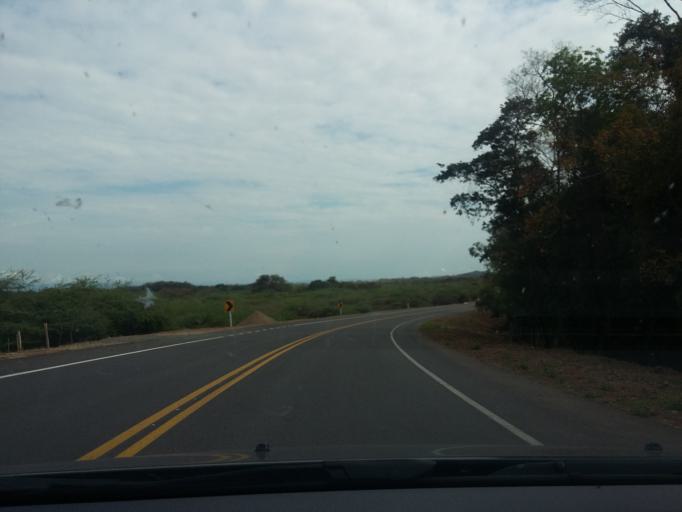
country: CO
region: Tolima
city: Ambalema
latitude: 4.6896
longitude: -74.7886
